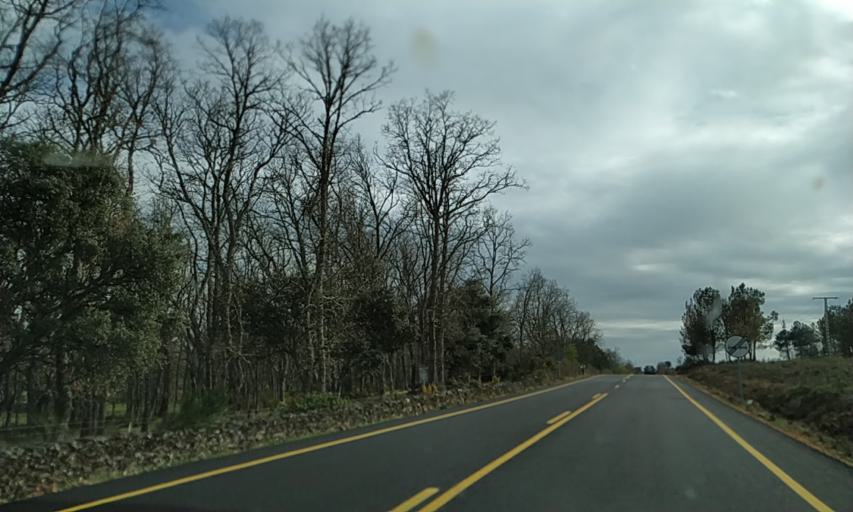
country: ES
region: Castille and Leon
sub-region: Provincia de Salamanca
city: Robleda
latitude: 40.3676
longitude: -6.6197
